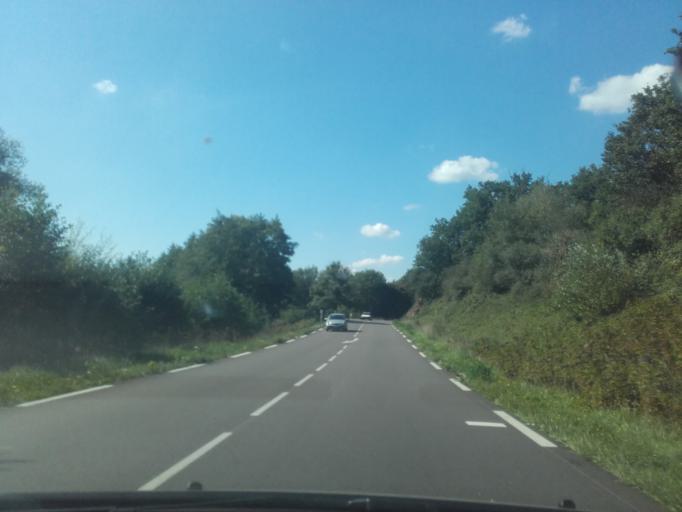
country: FR
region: Bourgogne
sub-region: Departement de Saone-et-Loire
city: Epinac
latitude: 46.9656
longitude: 4.5387
